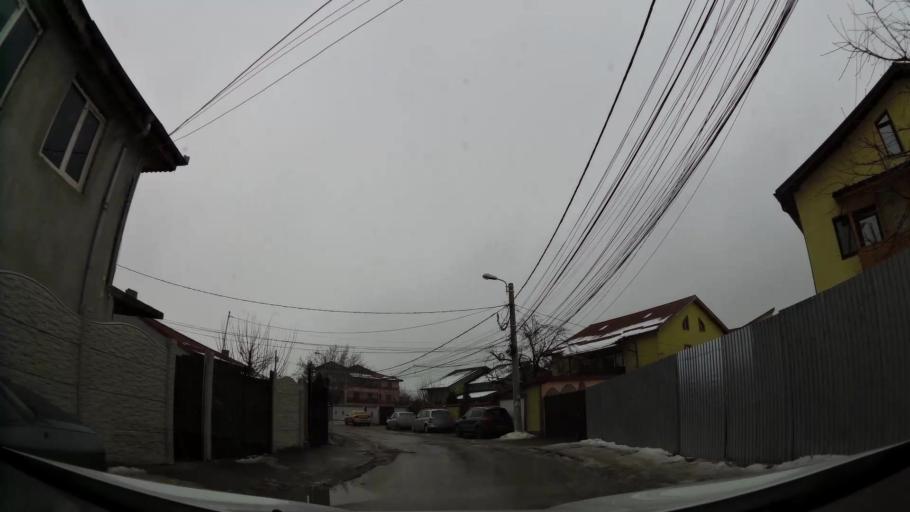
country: RO
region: Ilfov
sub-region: Comuna Popesti-Leordeni
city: Popesti-Leordeni
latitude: 44.4070
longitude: 26.1648
